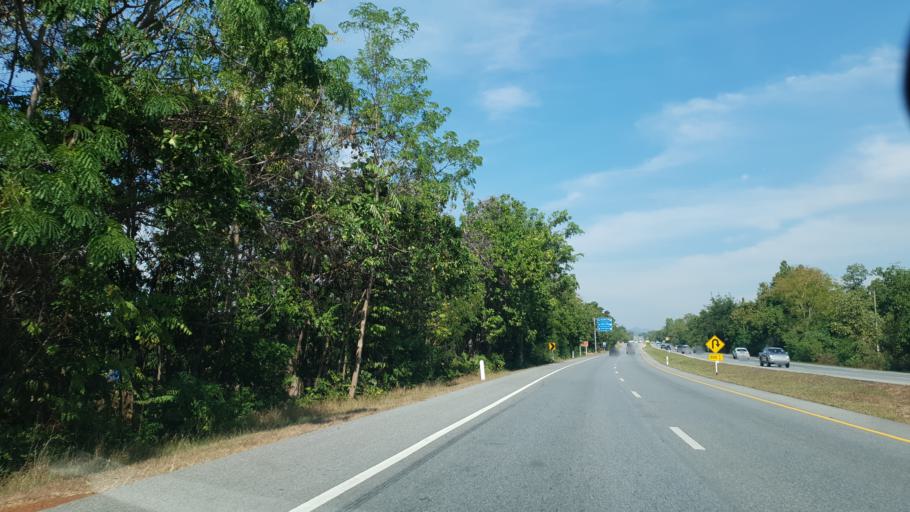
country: TH
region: Uttaradit
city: Thong Saen Khan
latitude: 17.4288
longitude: 100.2265
